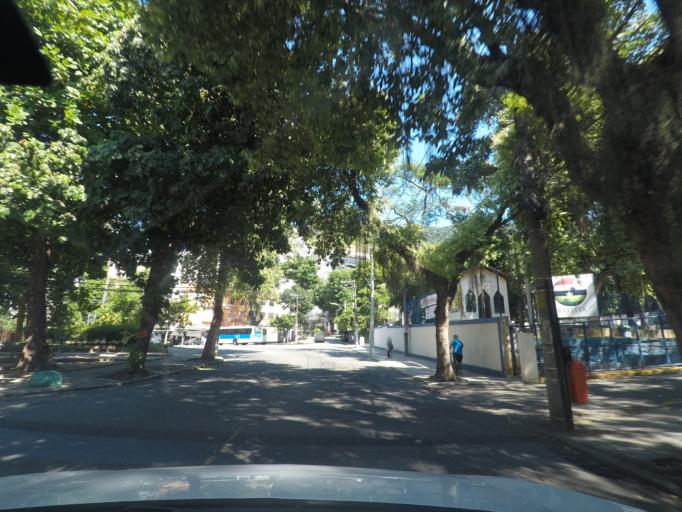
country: BR
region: Rio de Janeiro
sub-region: Rio De Janeiro
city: Rio de Janeiro
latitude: -22.9313
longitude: -43.2352
